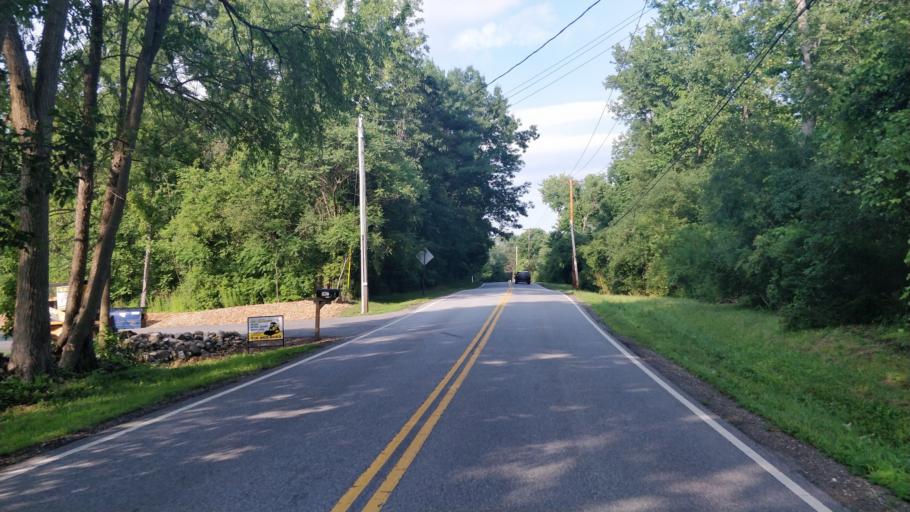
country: US
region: New York
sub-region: Saratoga County
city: North Ballston Spa
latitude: 43.0193
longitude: -73.8216
